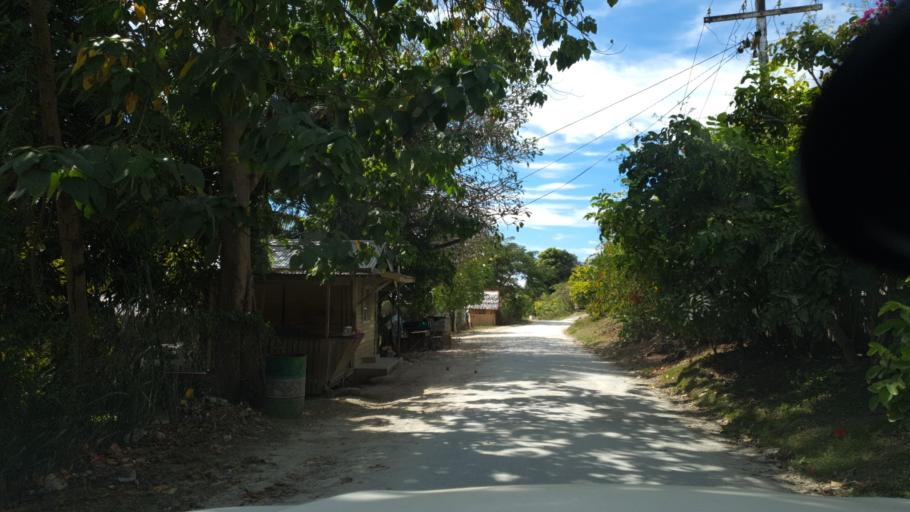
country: SB
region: Guadalcanal
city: Honiara
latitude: -9.4378
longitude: 159.9783
